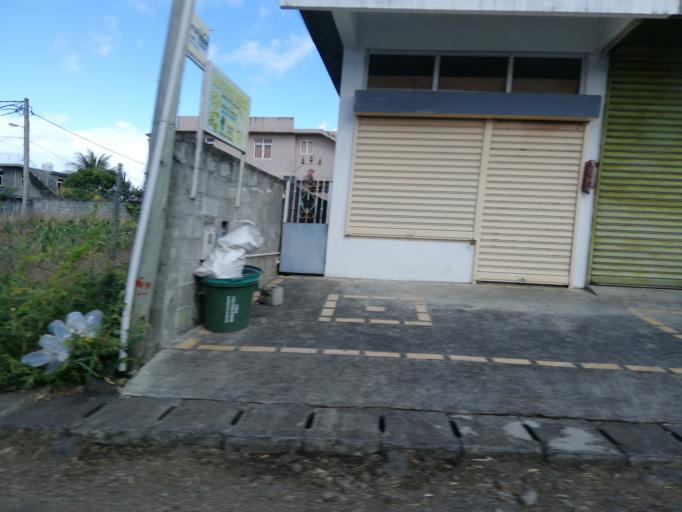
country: MU
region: Flacq
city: Bel Air Riviere Seche
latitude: -20.2621
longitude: 57.7429
